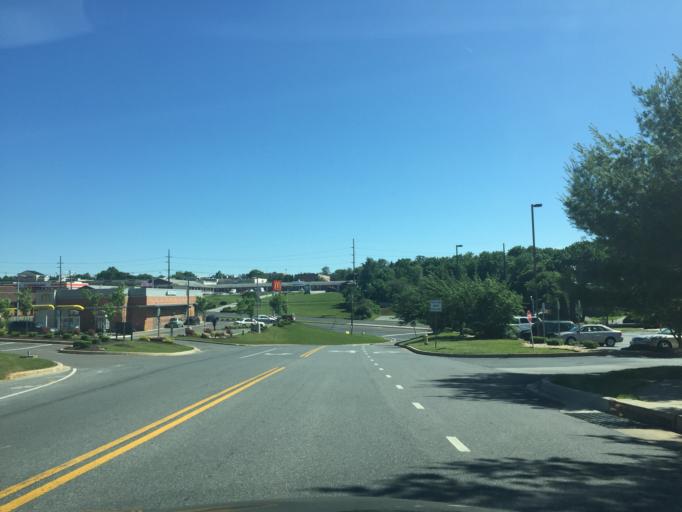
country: US
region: Maryland
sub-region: Carroll County
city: Westminster
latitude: 39.5690
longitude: -76.9787
